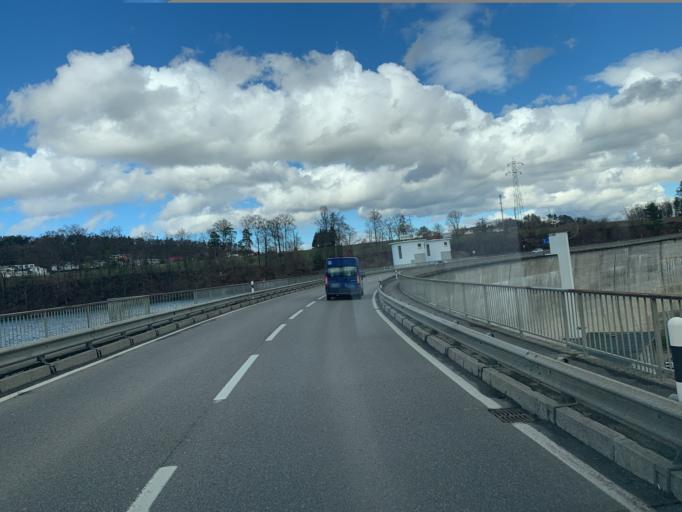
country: CH
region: Fribourg
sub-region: Sense District
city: Dudingen
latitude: 46.8815
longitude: 7.1932
